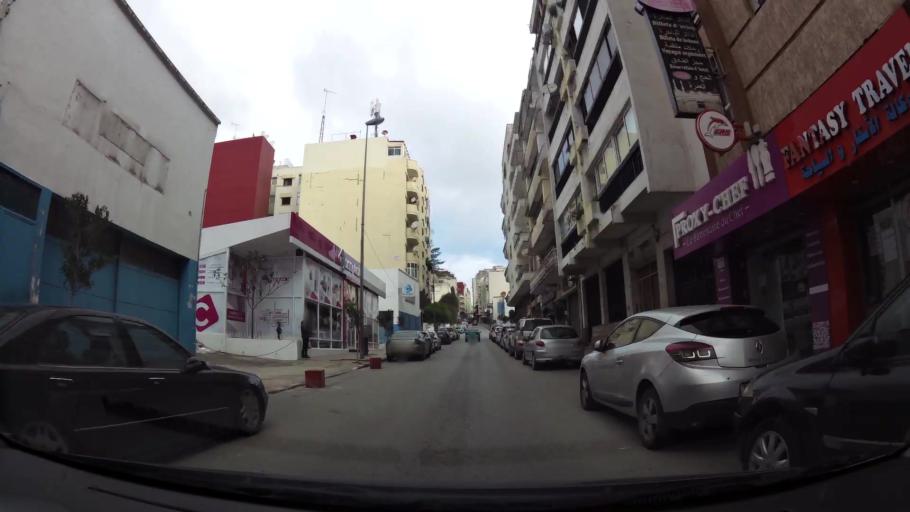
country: MA
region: Tanger-Tetouan
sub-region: Tanger-Assilah
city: Tangier
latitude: 35.7765
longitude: -5.8113
